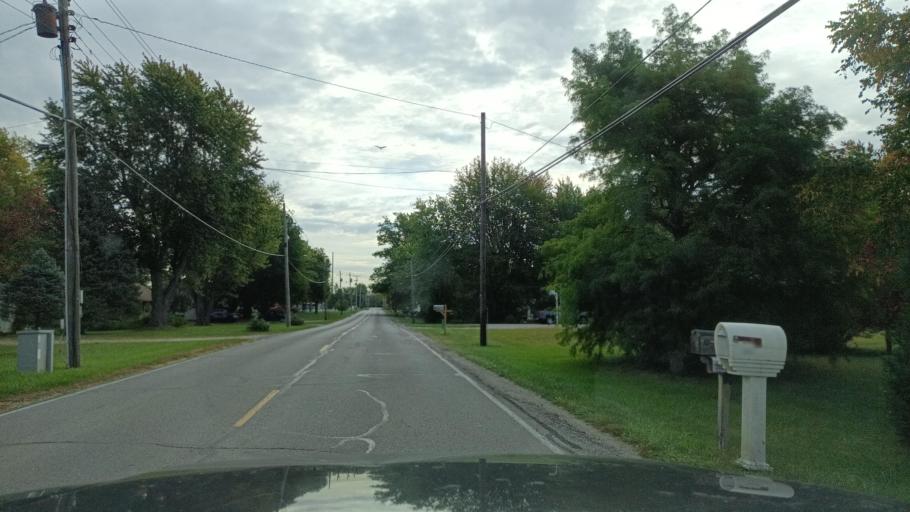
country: US
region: Indiana
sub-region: Delaware County
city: Yorktown
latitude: 40.2032
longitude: -85.4547
